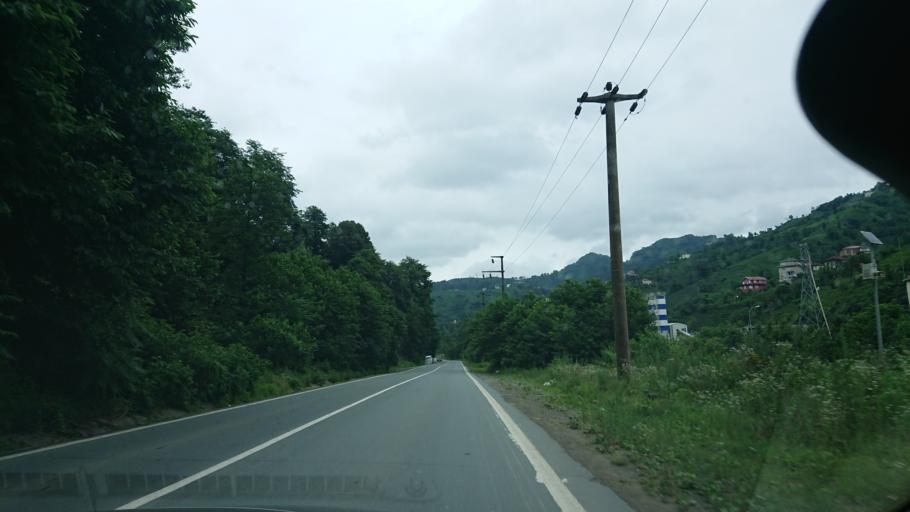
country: TR
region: Rize
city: Gundogdu
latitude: 41.0177
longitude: 40.5708
